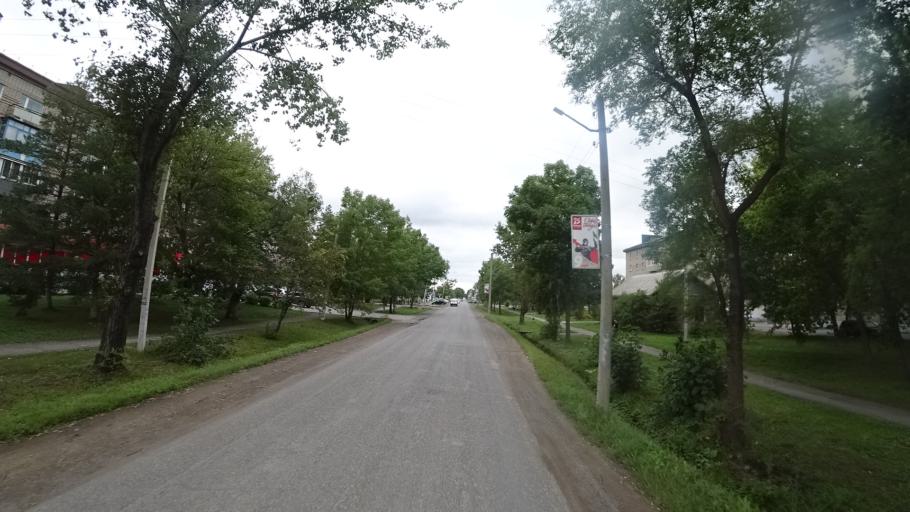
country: RU
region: Primorskiy
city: Chernigovka
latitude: 44.3422
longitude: 132.5769
